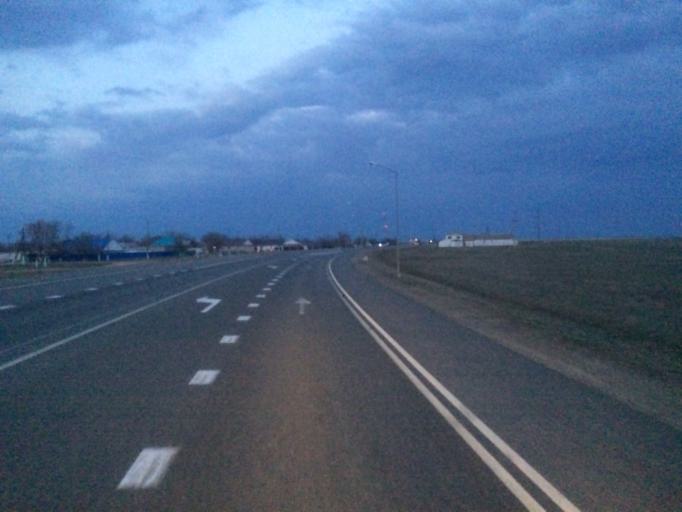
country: KZ
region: Aqtoebe
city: Martuk
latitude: 50.6399
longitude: 56.6888
